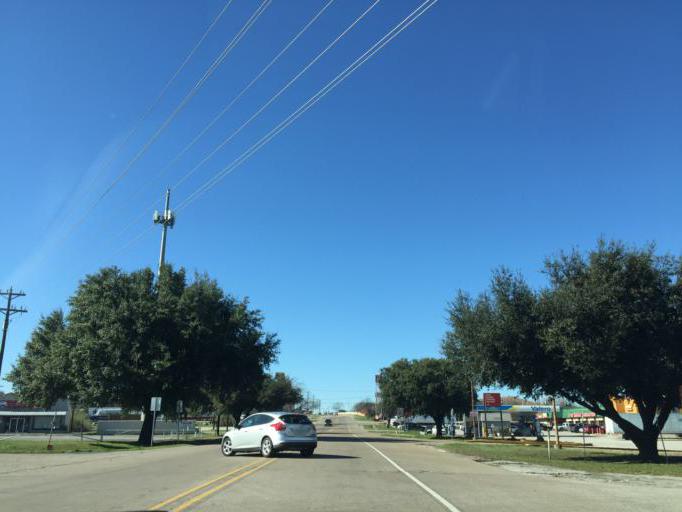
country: US
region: Texas
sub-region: Parker County
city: Weatherford
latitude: 32.7377
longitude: -97.7640
